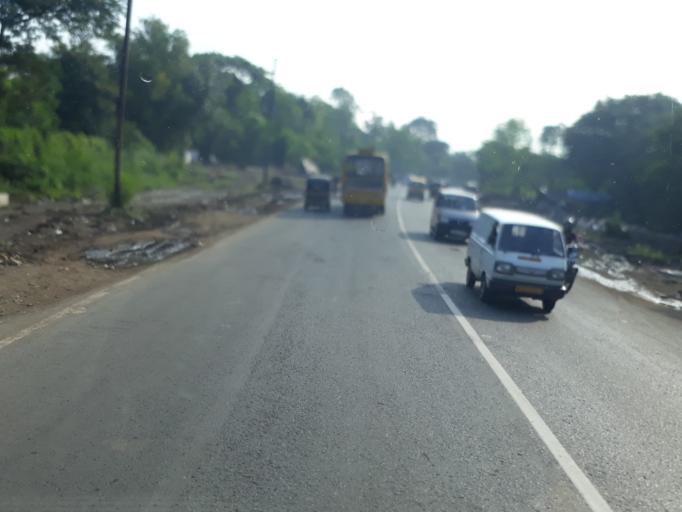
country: IN
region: Maharashtra
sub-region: Raigarh
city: Kalundri
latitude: 18.9752
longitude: 73.1211
